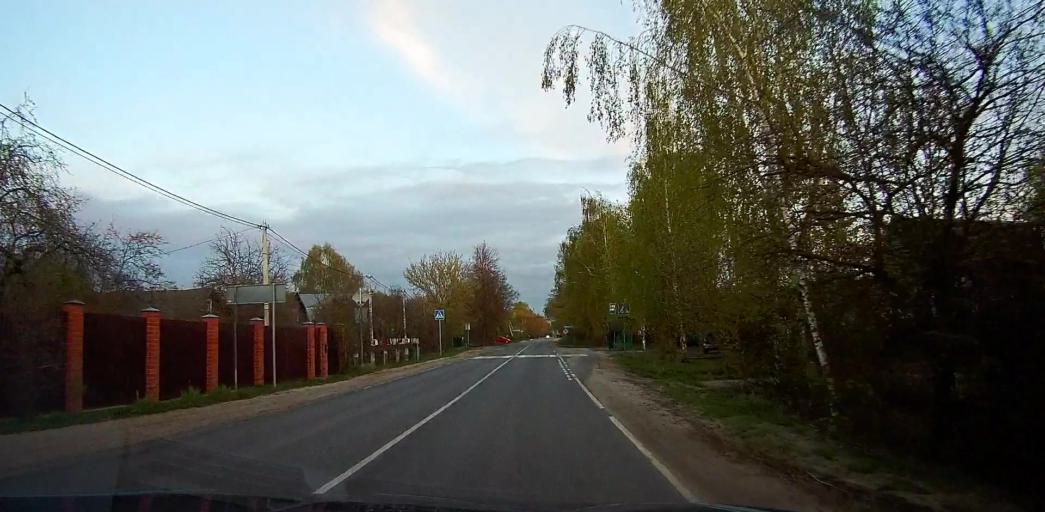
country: RU
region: Moskovskaya
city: Peski
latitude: 55.2077
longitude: 38.7393
